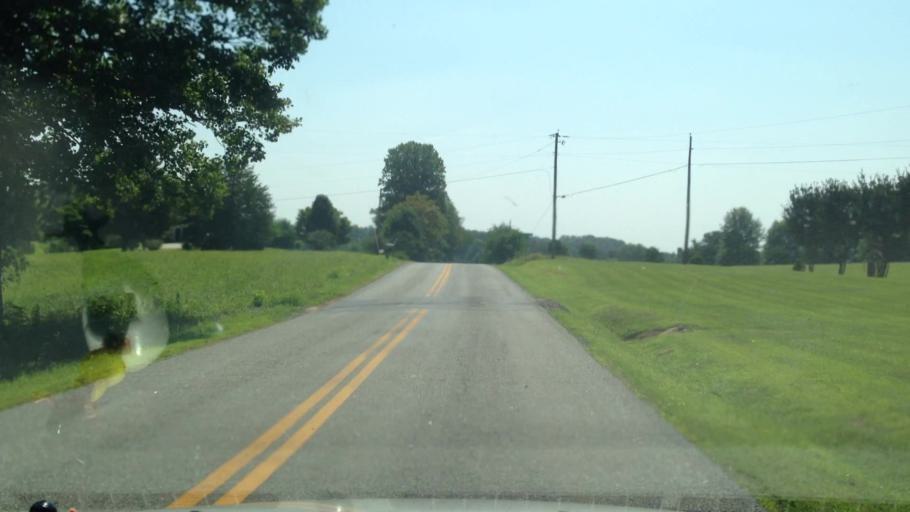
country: US
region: Virginia
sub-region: Patrick County
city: Stuart
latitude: 36.5784
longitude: -80.2553
